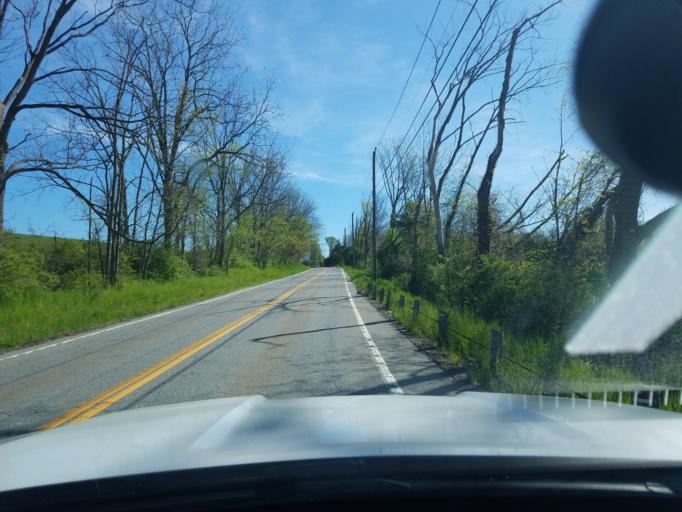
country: US
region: Connecticut
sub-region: Litchfield County
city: Kent
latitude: 41.8274
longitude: -73.5011
